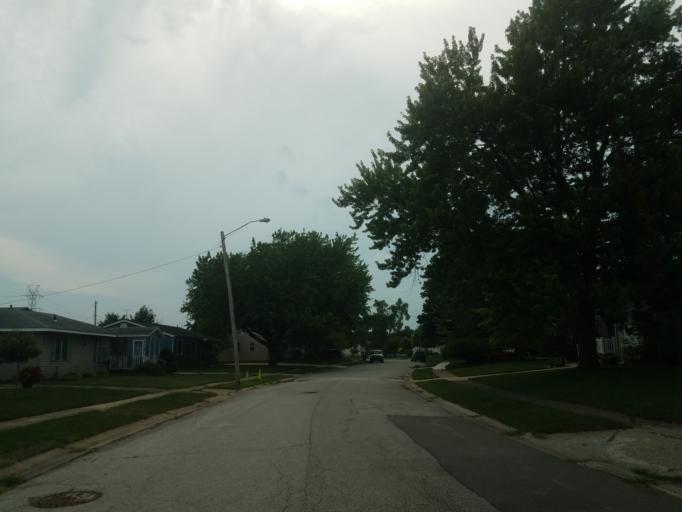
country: US
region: Illinois
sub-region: McLean County
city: Bloomington
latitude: 40.4634
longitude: -88.9701
